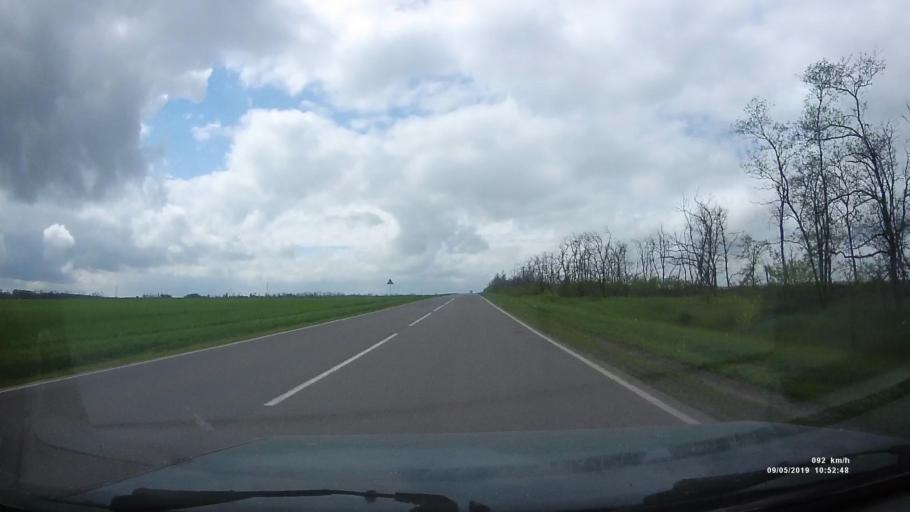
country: RU
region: Rostov
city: Peshkovo
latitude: 46.8964
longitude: 39.3491
